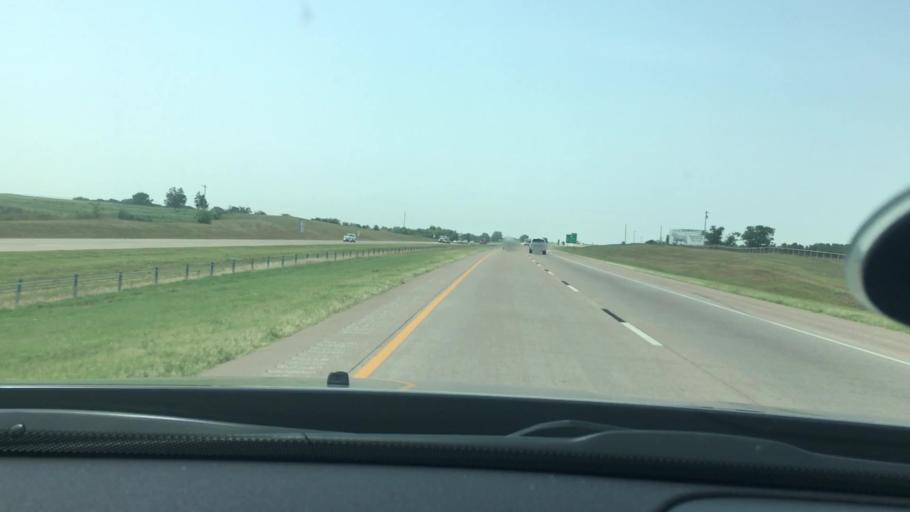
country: US
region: Oklahoma
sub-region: Garvin County
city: Wynnewood
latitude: 34.6617
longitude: -97.2220
